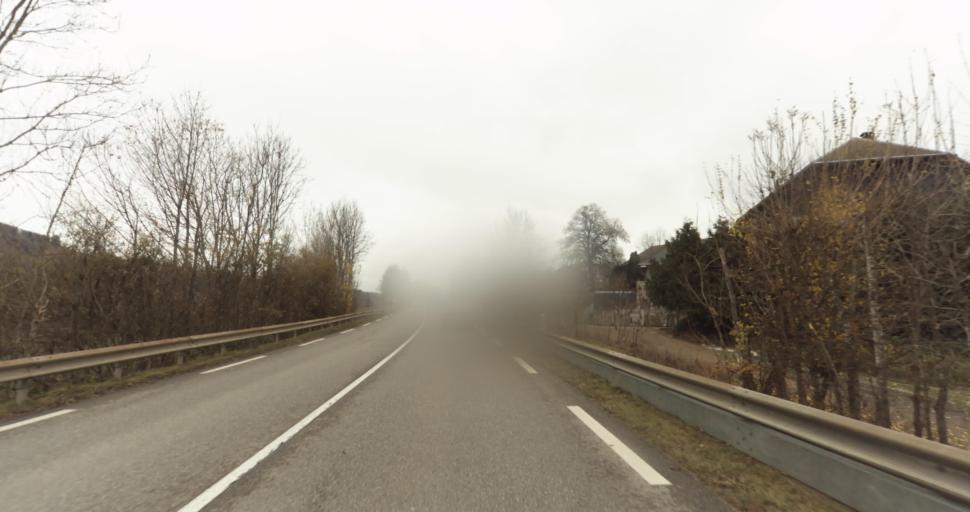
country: FR
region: Rhone-Alpes
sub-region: Departement de la Haute-Savoie
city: Evires
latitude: 46.0261
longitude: 6.2375
